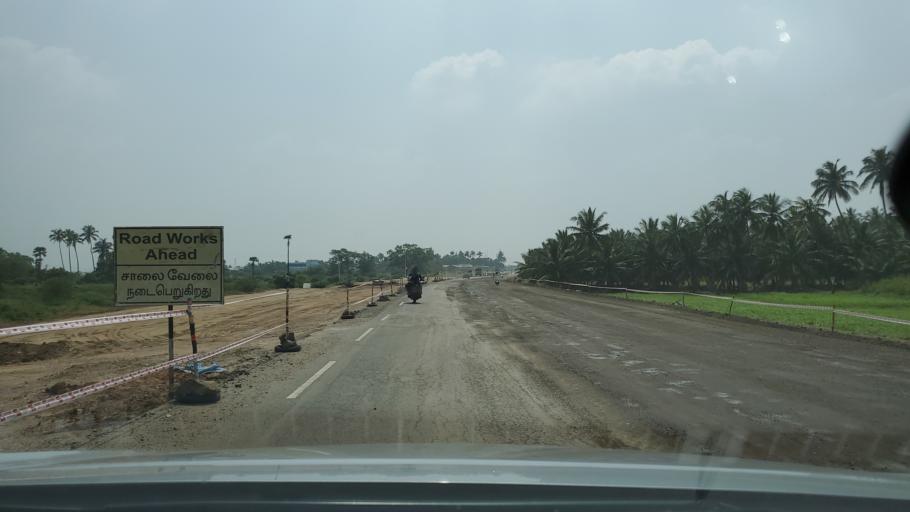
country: IN
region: Tamil Nadu
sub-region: Tiruppur
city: Kangayam
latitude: 10.9535
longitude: 77.4326
